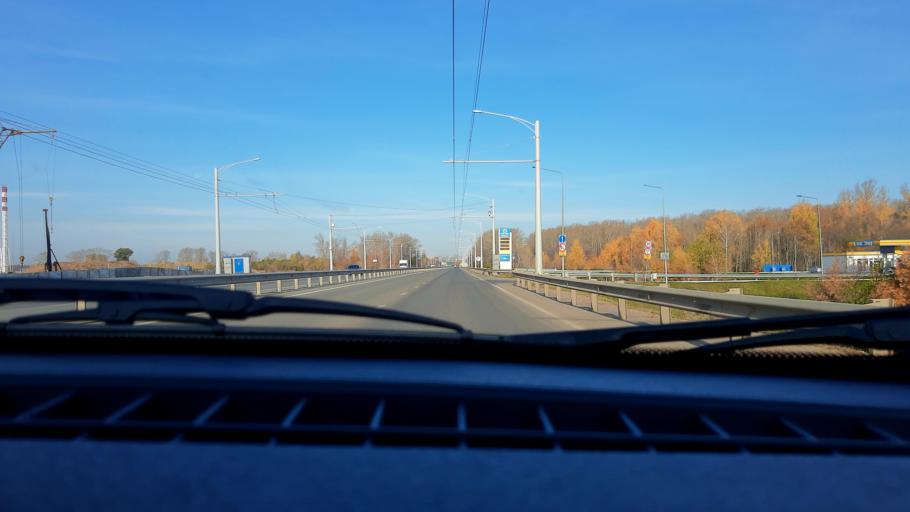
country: RU
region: Bashkortostan
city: Mikhaylovka
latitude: 54.7716
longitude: 55.9038
